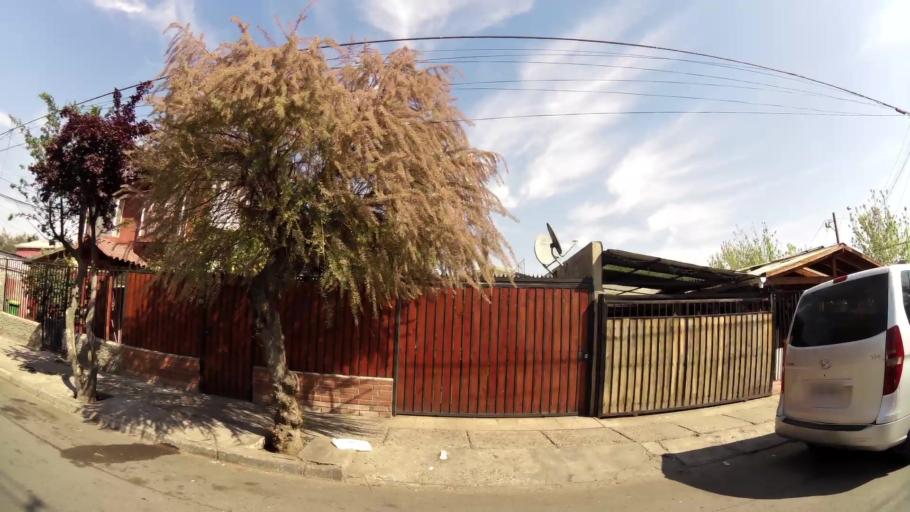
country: CL
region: Santiago Metropolitan
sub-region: Provincia de Santiago
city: La Pintana
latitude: -33.5624
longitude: -70.6521
